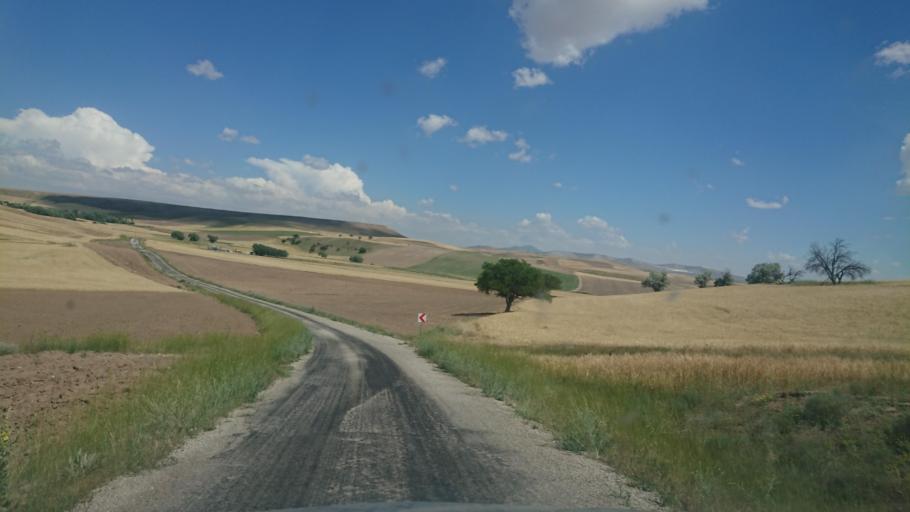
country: TR
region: Aksaray
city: Agacoren
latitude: 38.8004
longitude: 33.8174
